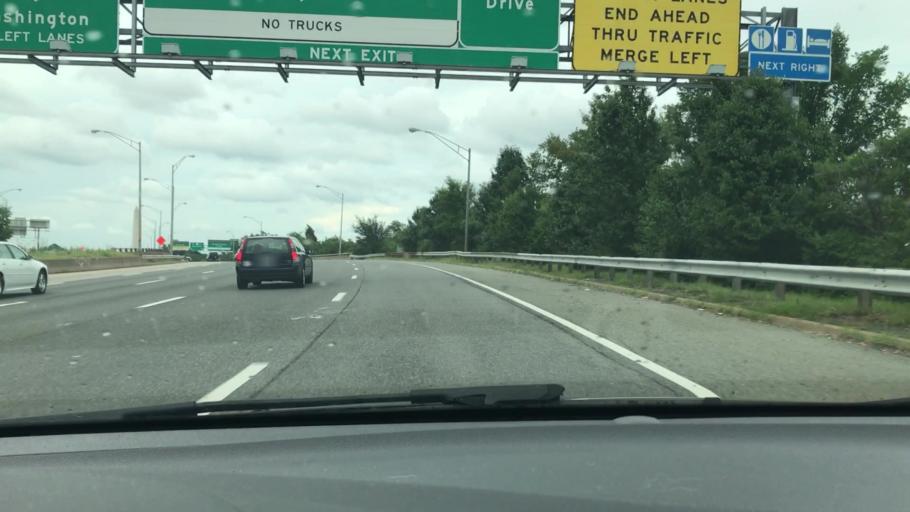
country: US
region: Washington, D.C.
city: Washington, D.C.
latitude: 38.8674
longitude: -77.0479
